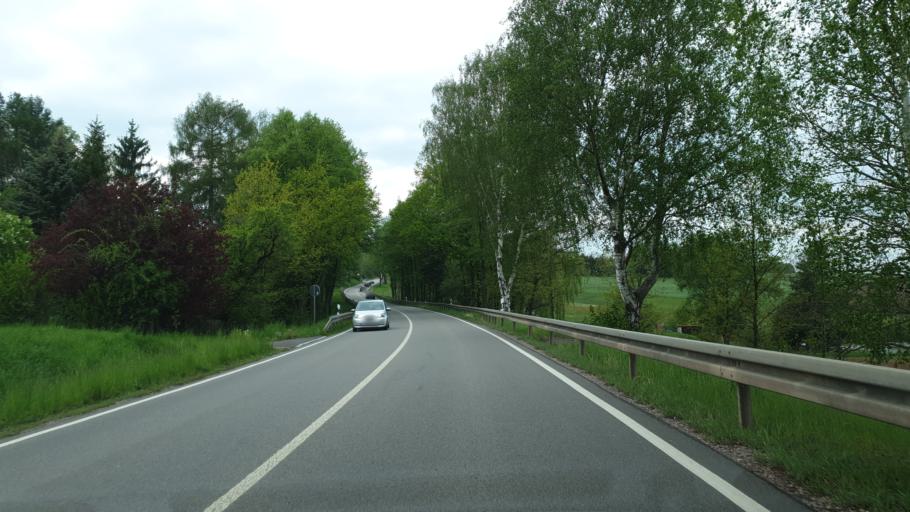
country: DE
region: Saxony
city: Bernsdorf
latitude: 50.7756
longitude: 12.6826
